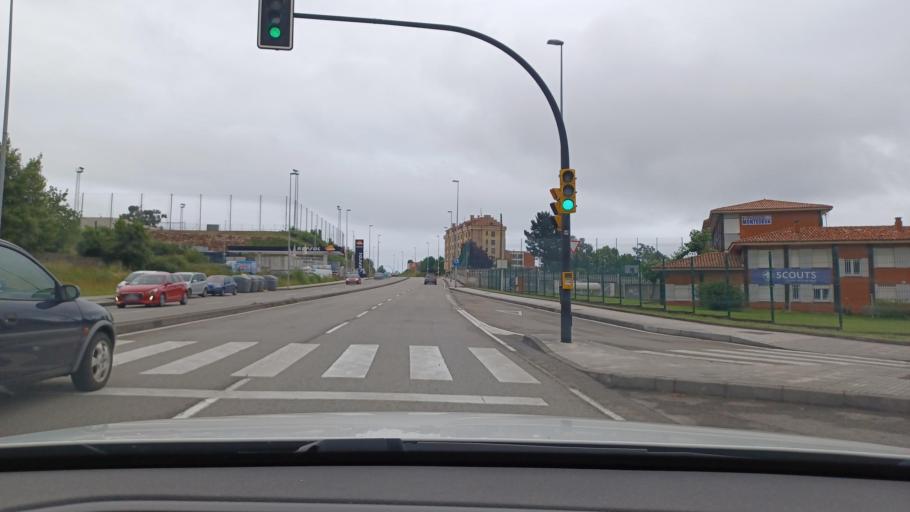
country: ES
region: Asturias
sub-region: Province of Asturias
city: Gijon
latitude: 43.5238
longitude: -5.6561
